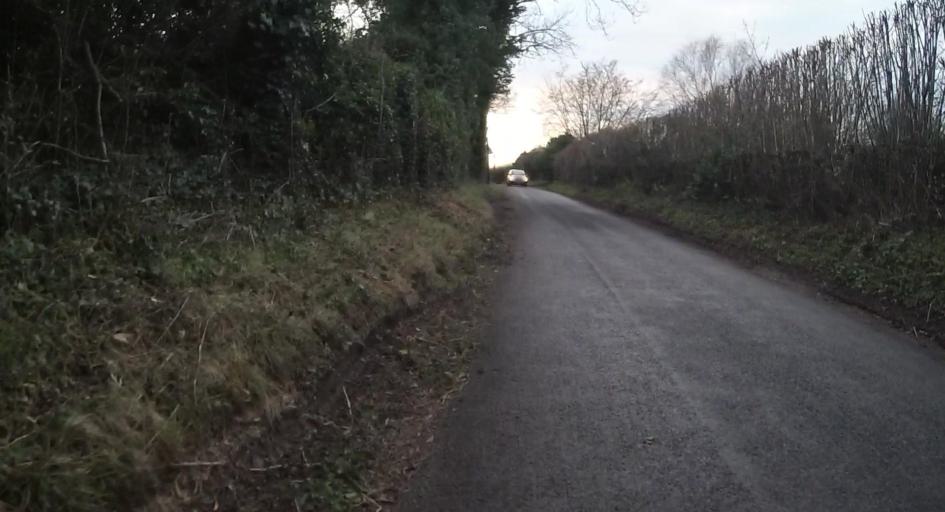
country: GB
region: England
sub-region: Hampshire
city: Swanmore
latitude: 51.0227
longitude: -1.1579
